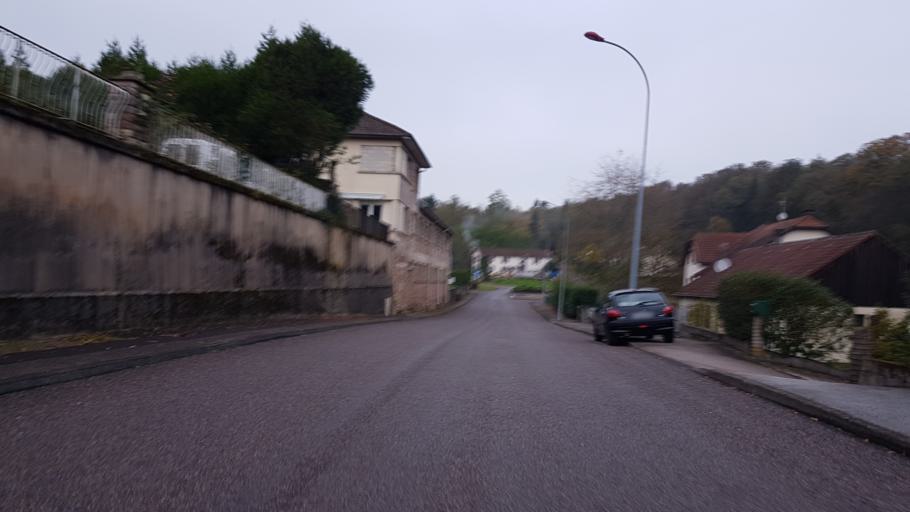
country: FR
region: Franche-Comte
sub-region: Departement de la Haute-Saone
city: Luxeuil-les-Bains
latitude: 47.8253
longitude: 6.3680
